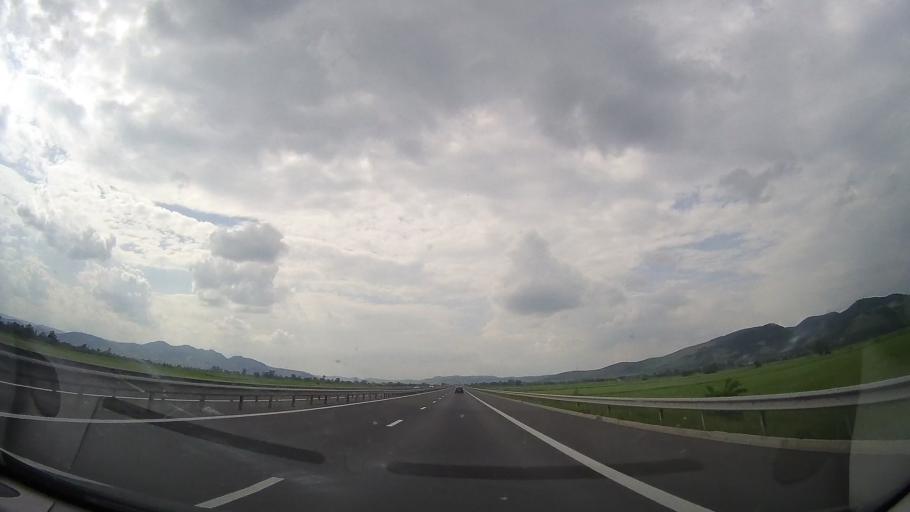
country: RO
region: Hunedoara
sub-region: Oras Simeria
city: Simeria
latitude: 45.8766
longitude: 23.0034
